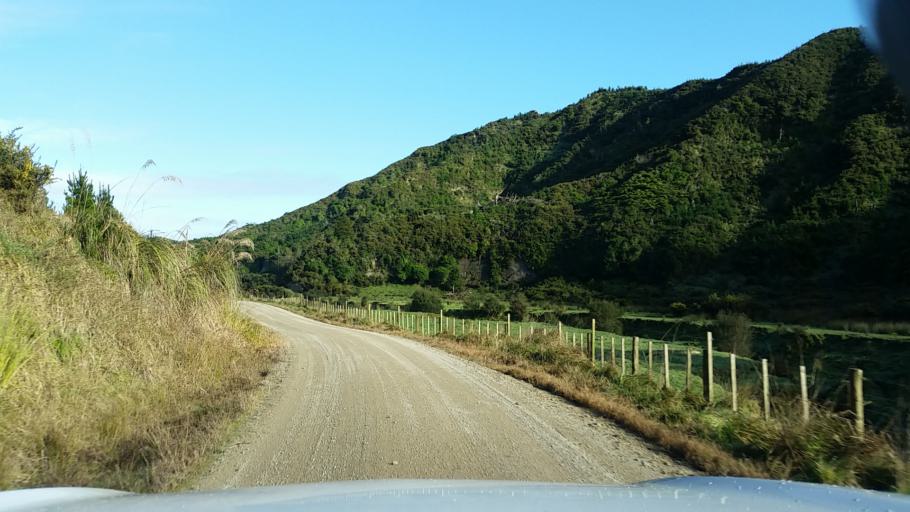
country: NZ
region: Taranaki
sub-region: South Taranaki District
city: Patea
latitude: -39.6927
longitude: 174.7493
